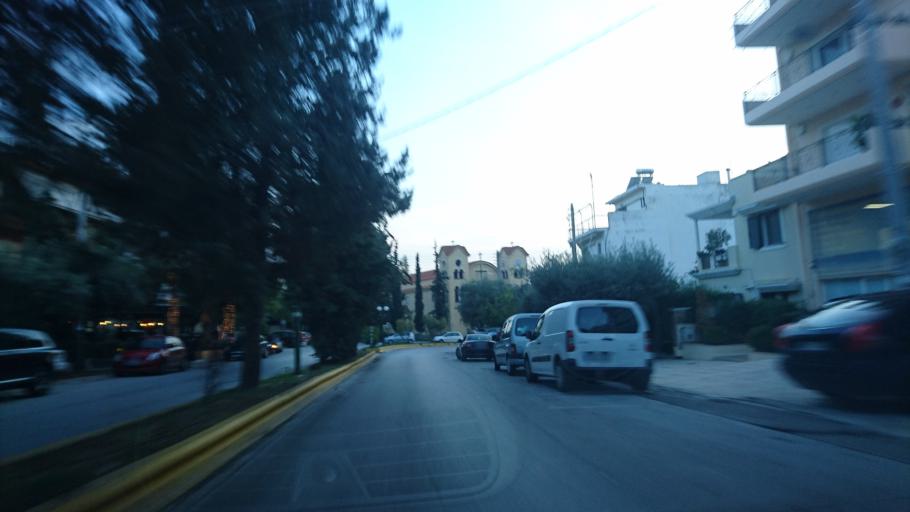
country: GR
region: Attica
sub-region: Nomarchia Athinas
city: Ilioupoli
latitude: 37.9251
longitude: 23.7519
